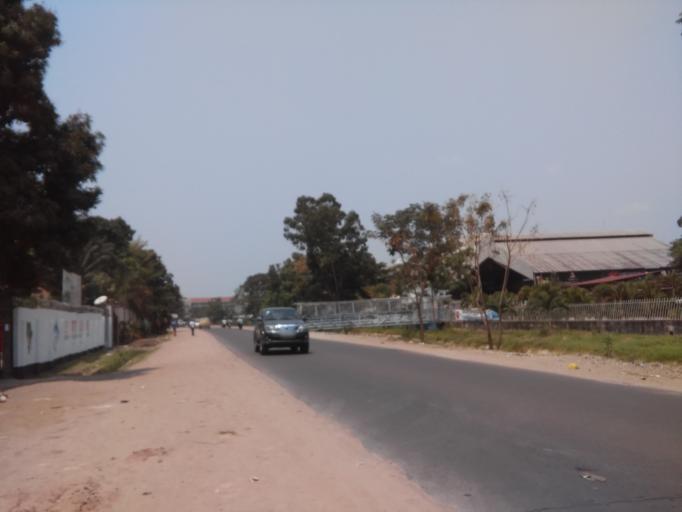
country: CD
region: Kinshasa
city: Kinshasa
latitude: -4.3182
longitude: 15.2869
